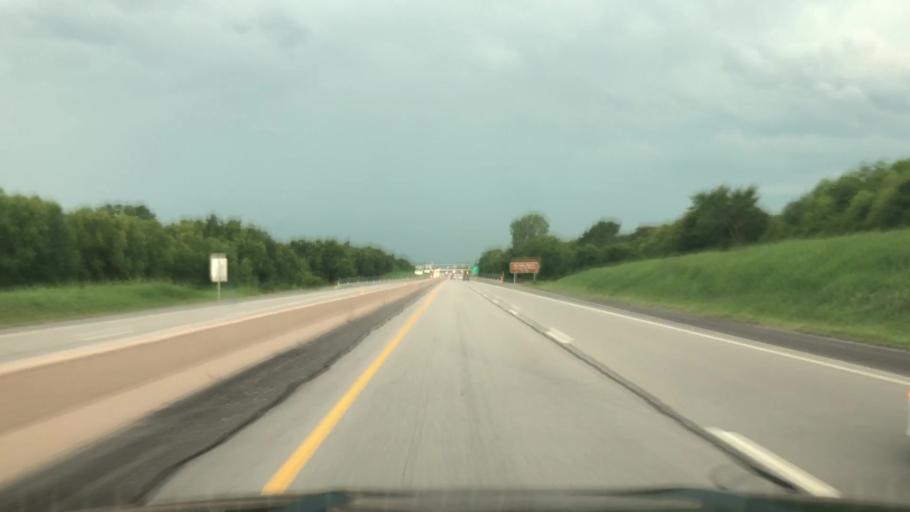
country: US
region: Oklahoma
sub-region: Rogers County
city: Justice
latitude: 36.3062
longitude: -95.5798
